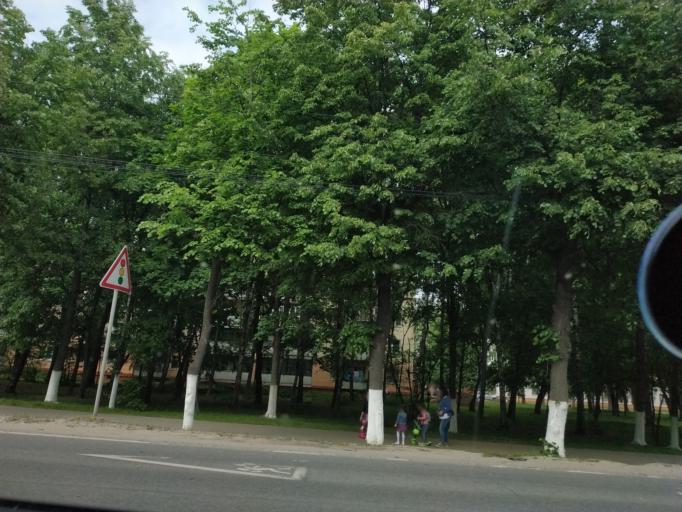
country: RU
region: Moskovskaya
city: Bronnitsy
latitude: 55.4227
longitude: 38.2726
